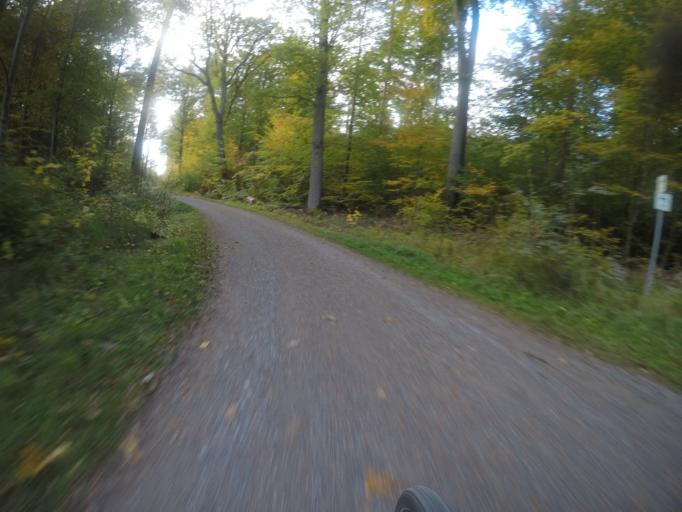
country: DE
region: Baden-Wuerttemberg
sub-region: Regierungsbezirk Stuttgart
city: Weil im Schonbuch
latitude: 48.6100
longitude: 9.0483
